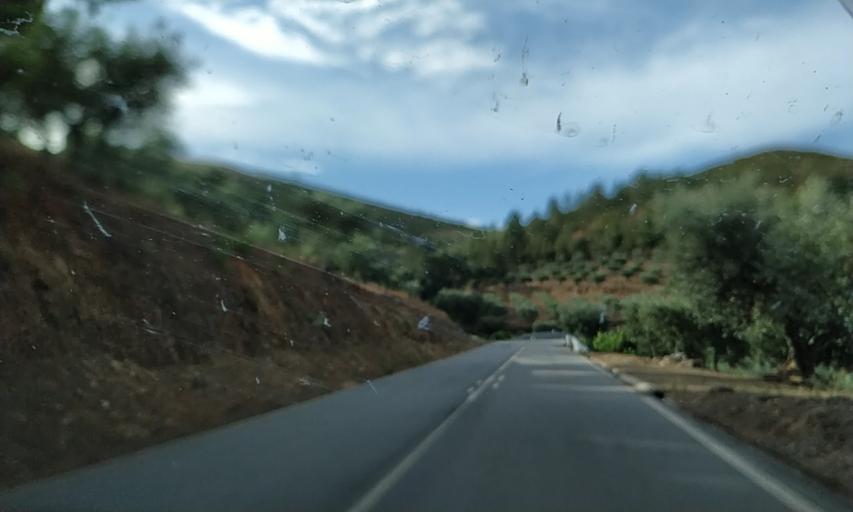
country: PT
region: Viseu
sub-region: Sao Joao da Pesqueira
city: Sao Joao da Pesqueira
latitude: 41.0994
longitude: -7.4620
